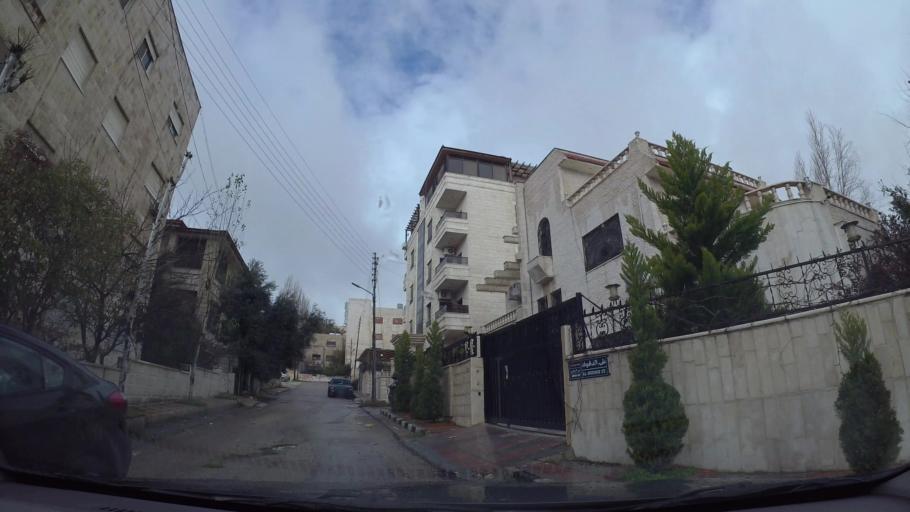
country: JO
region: Amman
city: Wadi as Sir
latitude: 31.9744
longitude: 35.8588
